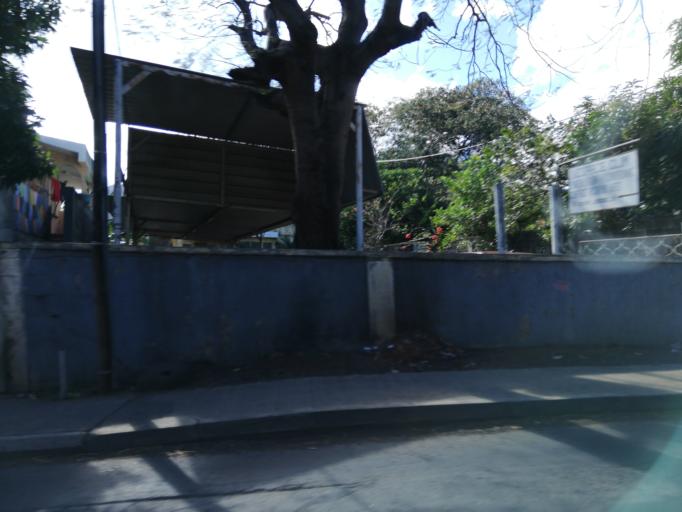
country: MU
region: Moka
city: Pailles
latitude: -20.1780
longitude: 57.4739
